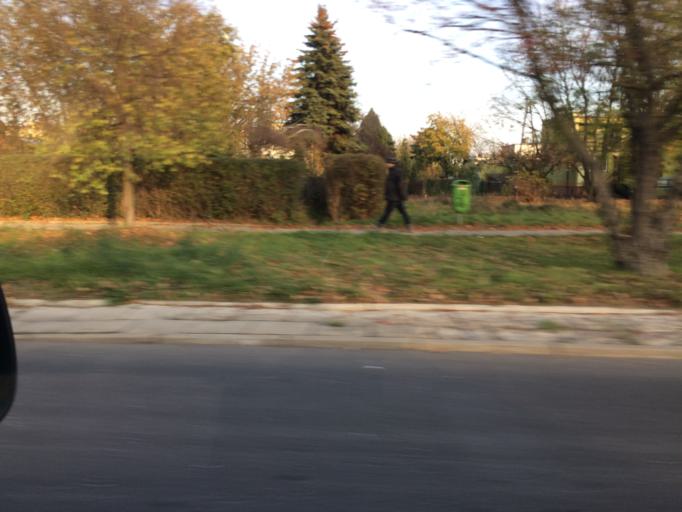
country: PL
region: Opole Voivodeship
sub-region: Powiat opolski
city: Opole
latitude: 50.6728
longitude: 17.9753
